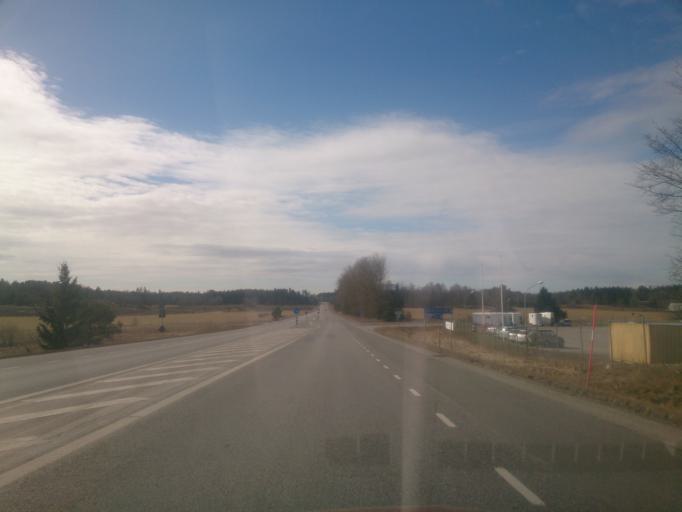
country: SE
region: OEstergoetland
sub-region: Norrkopings Kommun
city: Kimstad
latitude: 58.5016
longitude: 15.9740
